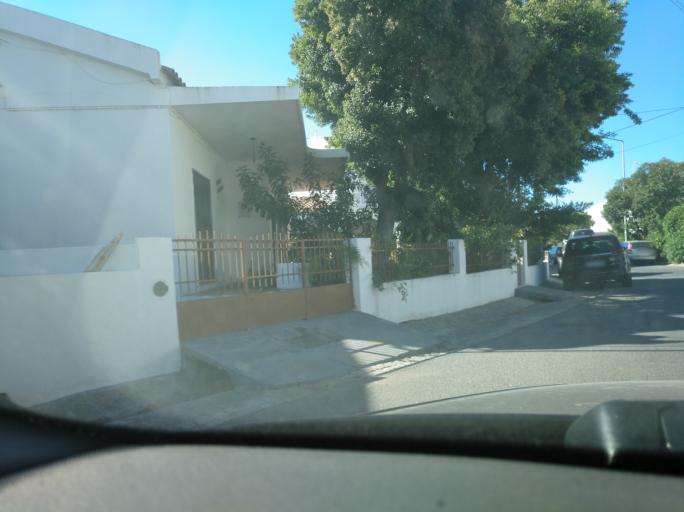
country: PT
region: Faro
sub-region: Vila Real de Santo Antonio
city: Monte Gordo
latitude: 37.1680
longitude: -7.5193
